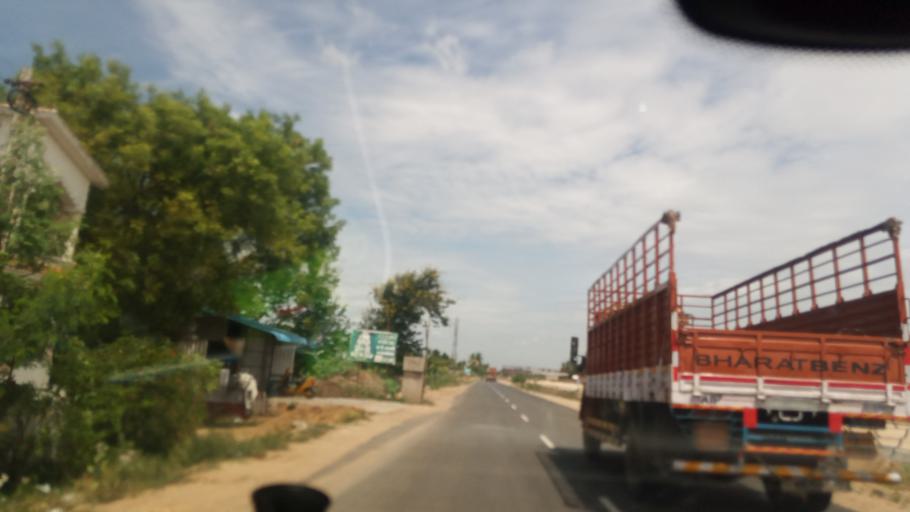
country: IN
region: Tamil Nadu
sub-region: Kancheepuram
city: Kanchipuram
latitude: 12.8979
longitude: 79.5612
